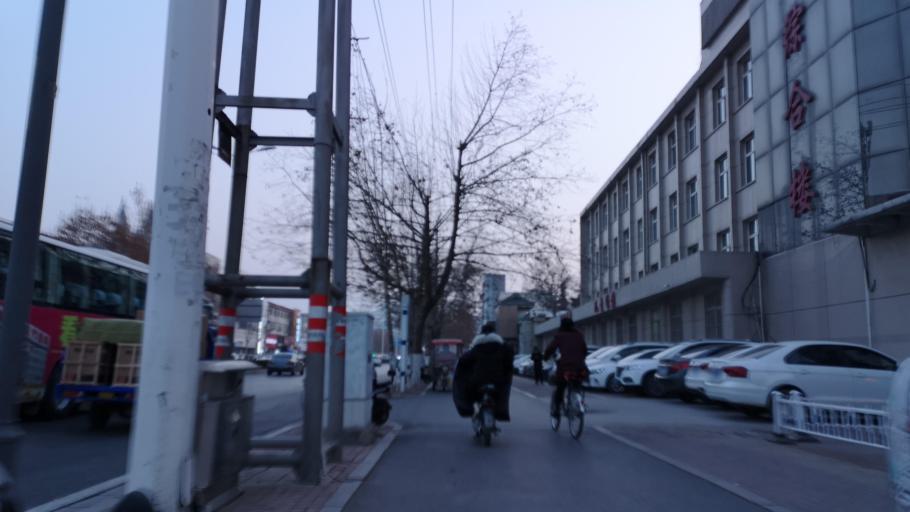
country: CN
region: Henan Sheng
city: Zhongyuanlu
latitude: 35.7729
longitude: 115.0698
